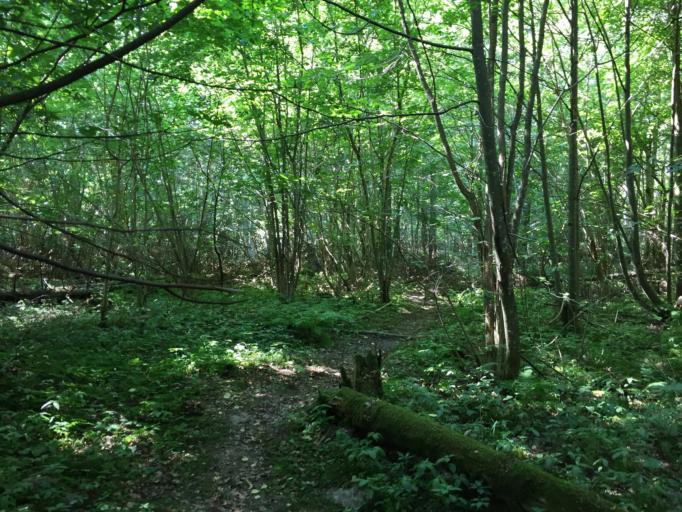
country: LT
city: Zagare
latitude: 56.3835
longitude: 23.2078
